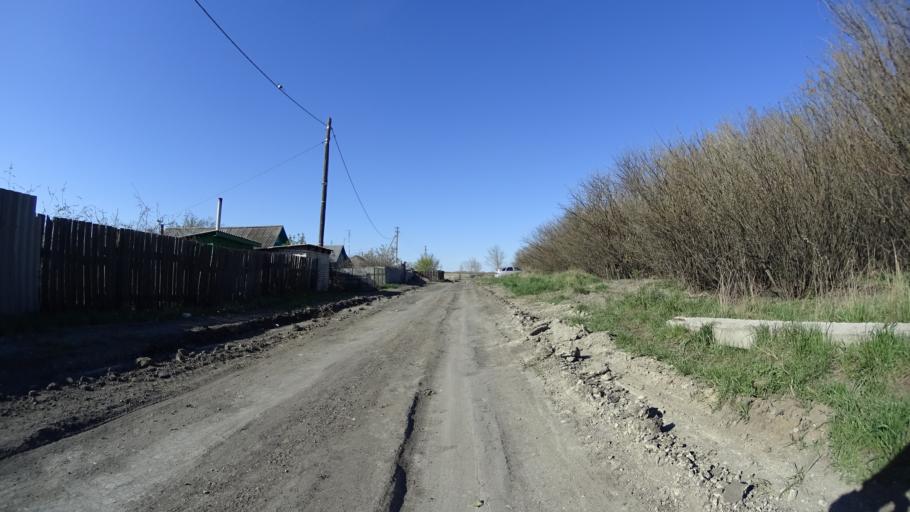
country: RU
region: Chelyabinsk
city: Troitsk
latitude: 54.0885
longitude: 61.5995
